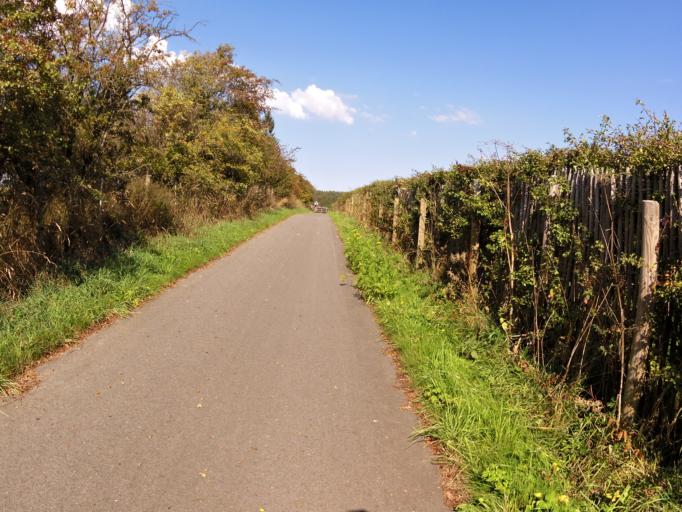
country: BE
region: Wallonia
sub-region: Province de Liege
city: Butgenbach
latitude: 50.4868
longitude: 6.1581
